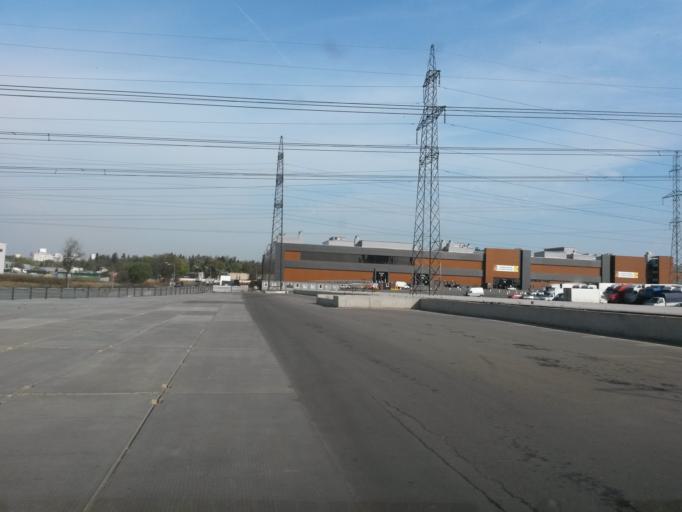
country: RU
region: Moskovskaya
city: Mosrentgen
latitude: 55.6001
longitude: 37.4637
